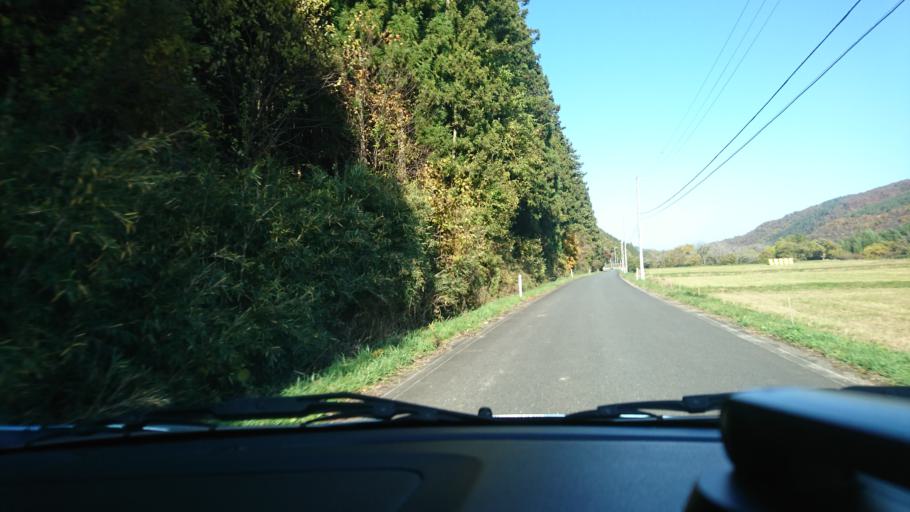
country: JP
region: Iwate
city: Ichinoseki
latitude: 38.8074
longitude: 141.2465
